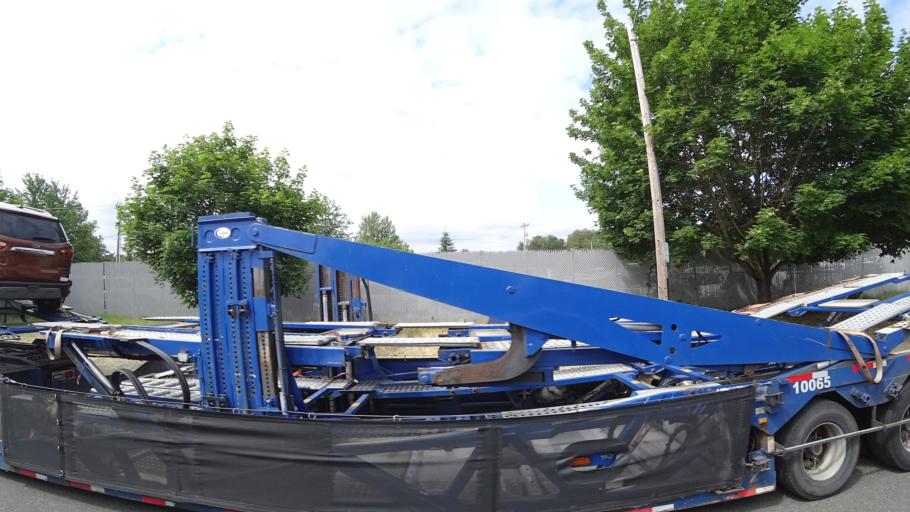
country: US
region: Washington
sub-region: Clark County
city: Vancouver
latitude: 45.6199
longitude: -122.6935
